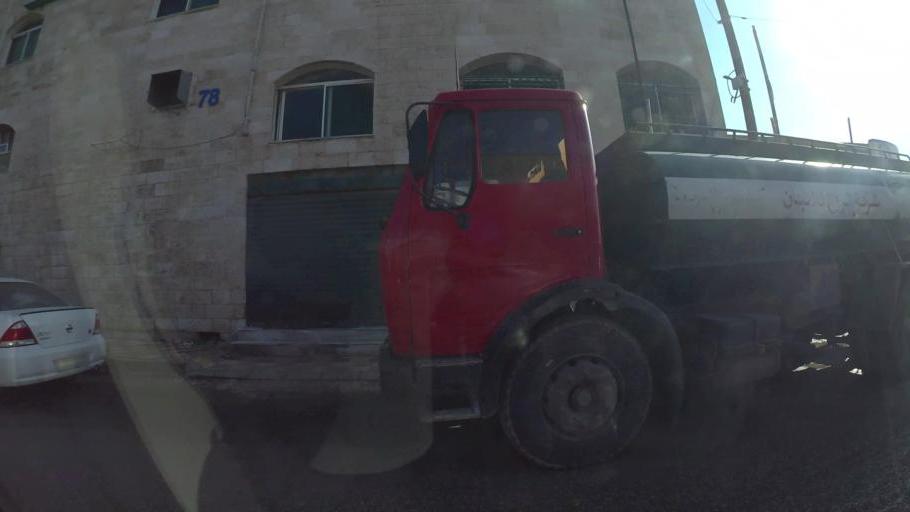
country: JO
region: Amman
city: Al Jubayhah
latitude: 32.0160
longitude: 35.8475
